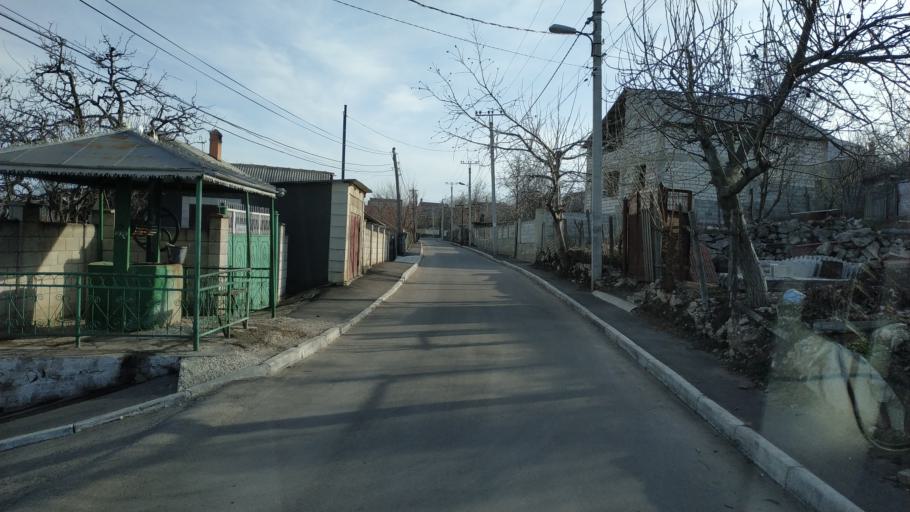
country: MD
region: Chisinau
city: Vatra
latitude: 47.0762
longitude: 28.6705
